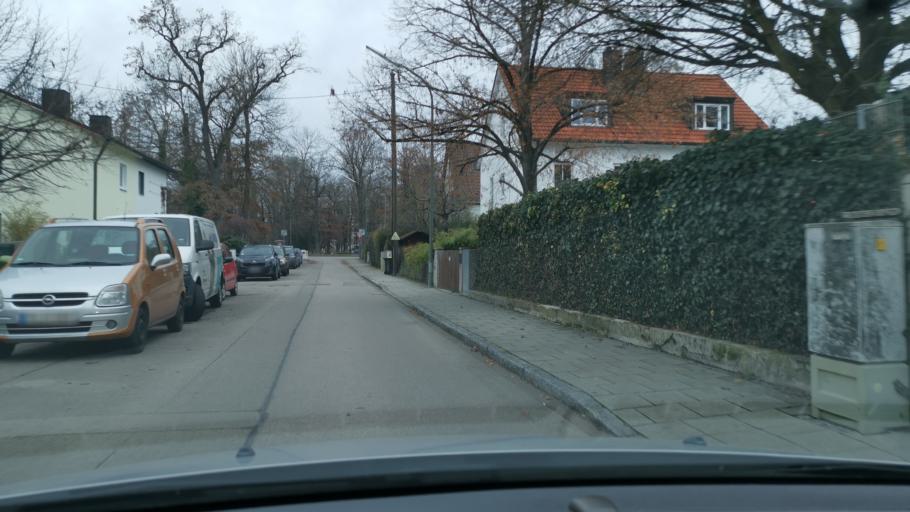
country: DE
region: Bavaria
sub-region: Upper Bavaria
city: Unterschleissheim
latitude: 48.2852
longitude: 11.5840
